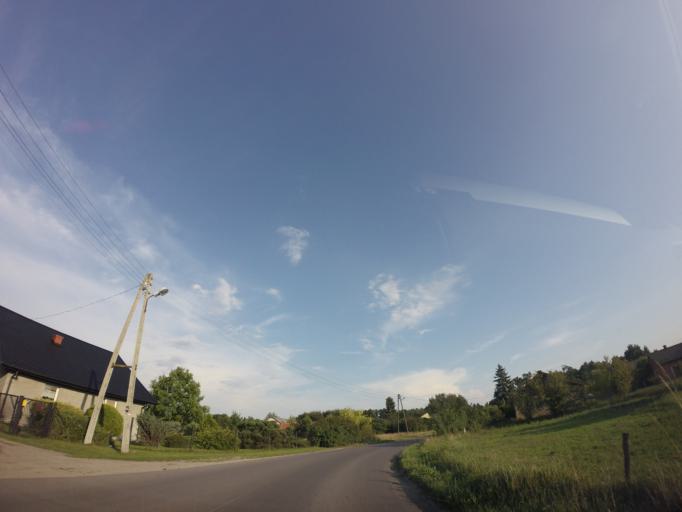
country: PL
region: Lublin Voivodeship
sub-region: Powiat pulawski
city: Kurow
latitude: 51.4221
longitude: 22.2287
